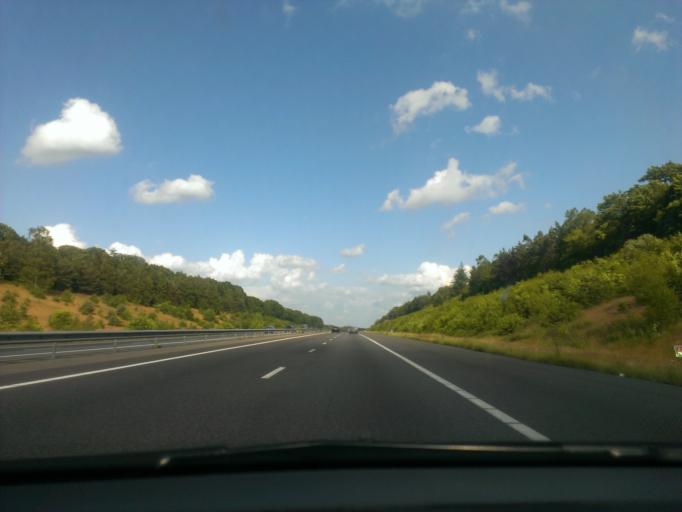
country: NL
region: Gelderland
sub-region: Gemeente Apeldoorn
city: Beekbergen
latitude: 52.1874
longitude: 5.8616
